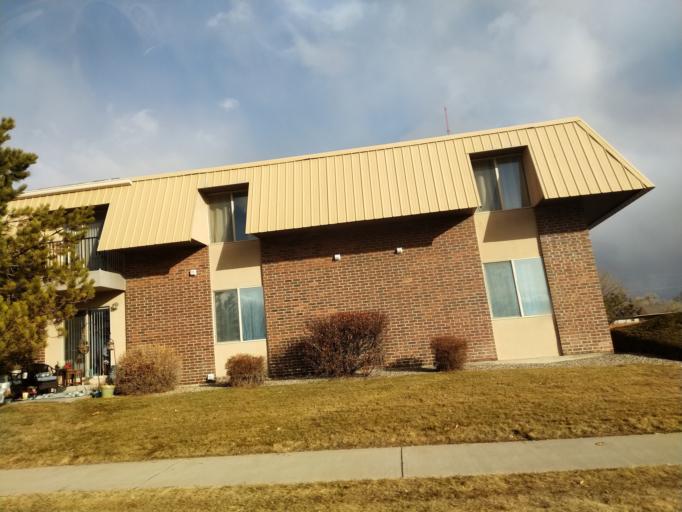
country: US
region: Colorado
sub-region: Mesa County
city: Grand Junction
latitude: 39.0949
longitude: -108.5802
